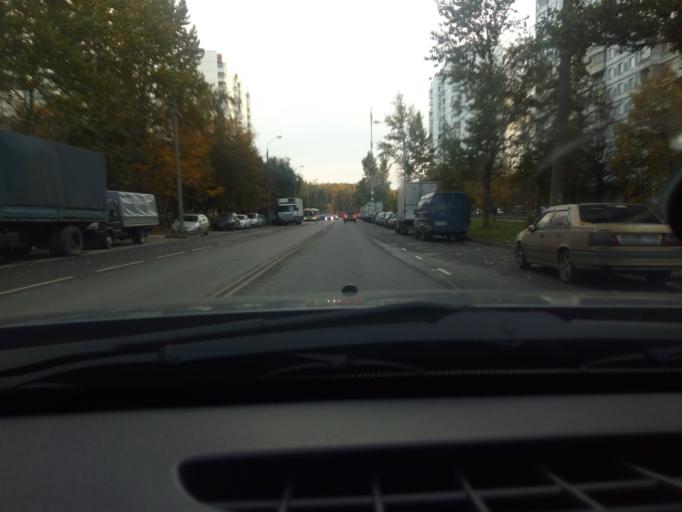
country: RU
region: Moskovskaya
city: Reutov
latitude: 55.7407
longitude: 37.8668
